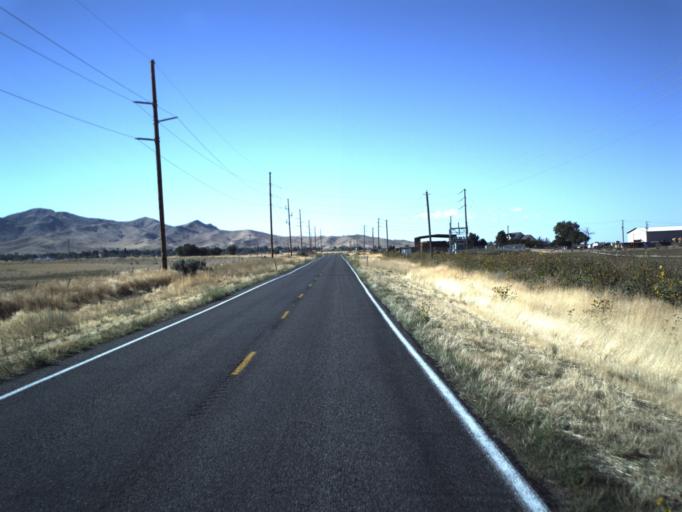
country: US
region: Utah
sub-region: Millard County
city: Delta
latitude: 39.4058
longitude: -112.3333
